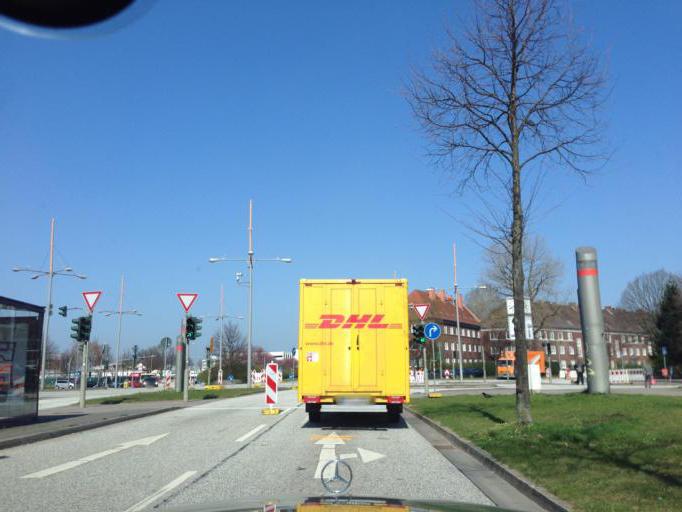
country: DE
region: Hamburg
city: Fuhlsbuettel
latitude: 53.6233
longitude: 10.0120
